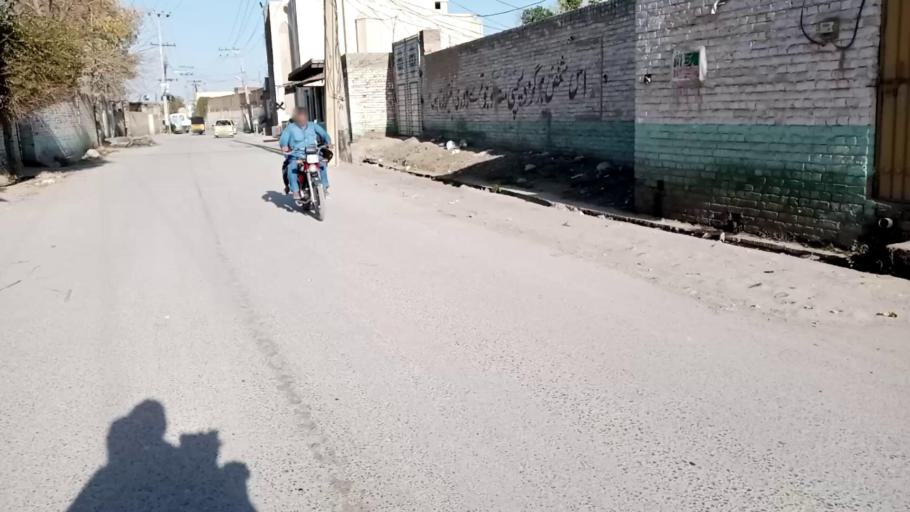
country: PK
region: Khyber Pakhtunkhwa
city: Peshawar
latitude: 34.0543
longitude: 71.5334
